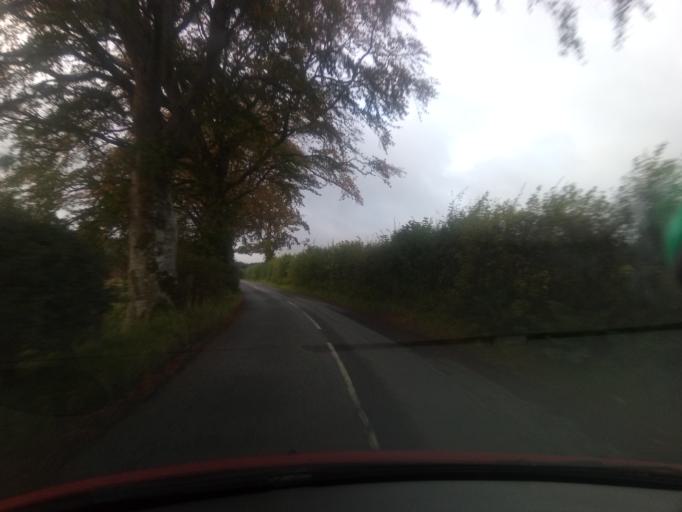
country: GB
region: Scotland
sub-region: The Scottish Borders
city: Hawick
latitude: 55.3432
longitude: -2.6511
